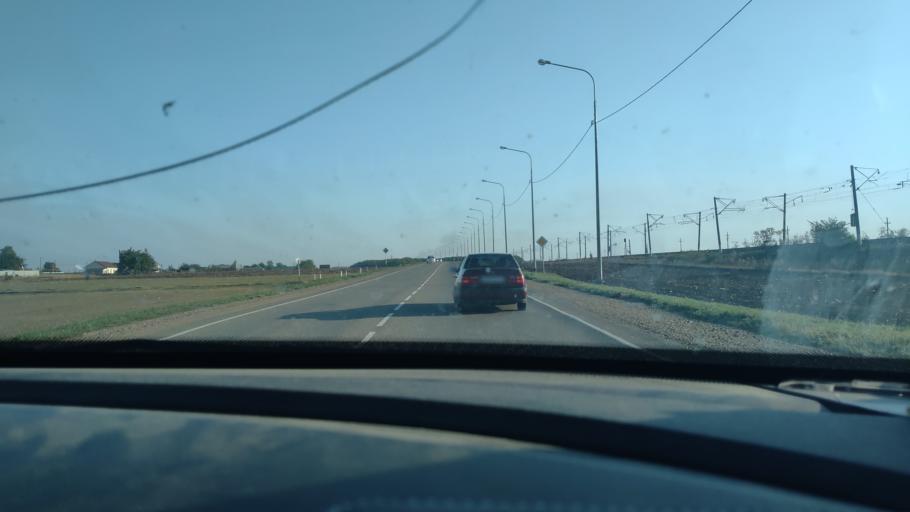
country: RU
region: Krasnodarskiy
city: Novominskaya
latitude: 46.3116
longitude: 38.9306
